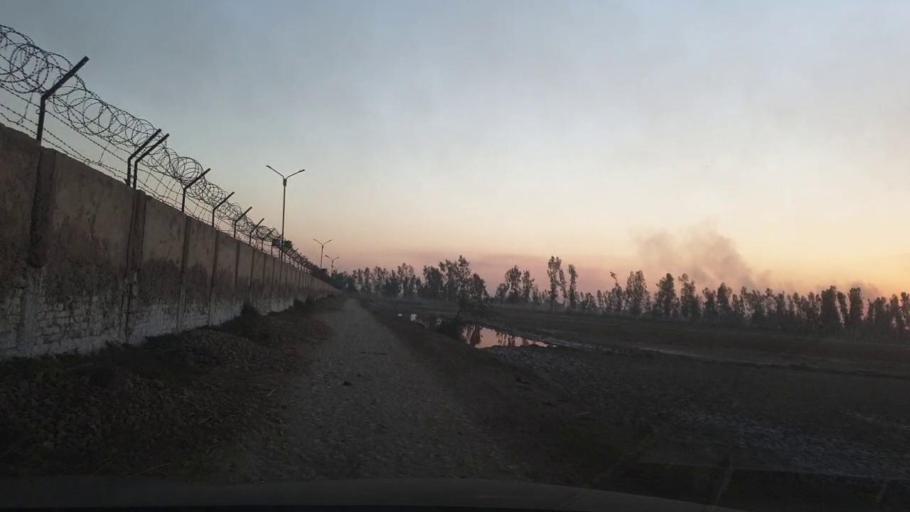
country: PK
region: Sindh
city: Ghotki
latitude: 28.0469
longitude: 69.3575
